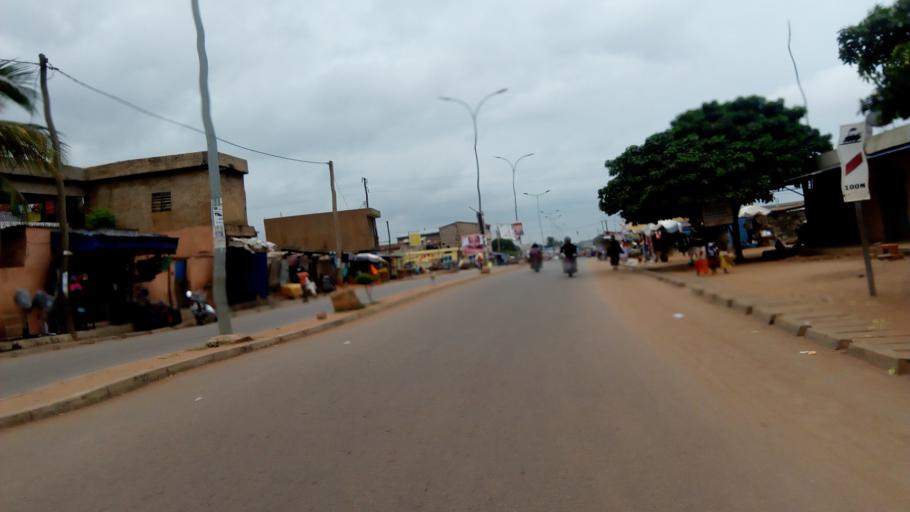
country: TG
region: Maritime
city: Lome
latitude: 6.2207
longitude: 1.2063
